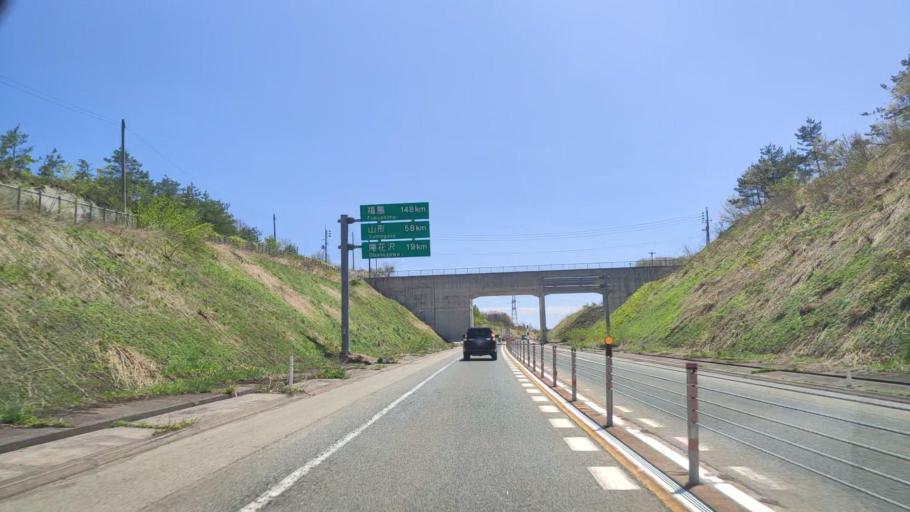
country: JP
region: Yamagata
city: Shinjo
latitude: 38.7230
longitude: 140.3083
